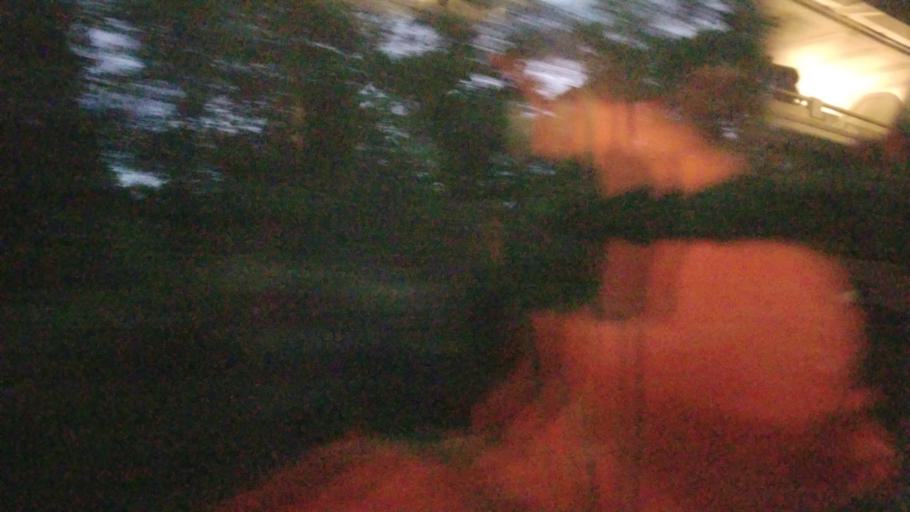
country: US
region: Virginia
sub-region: Greene County
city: Ruckersville
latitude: 38.1609
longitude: -78.3451
